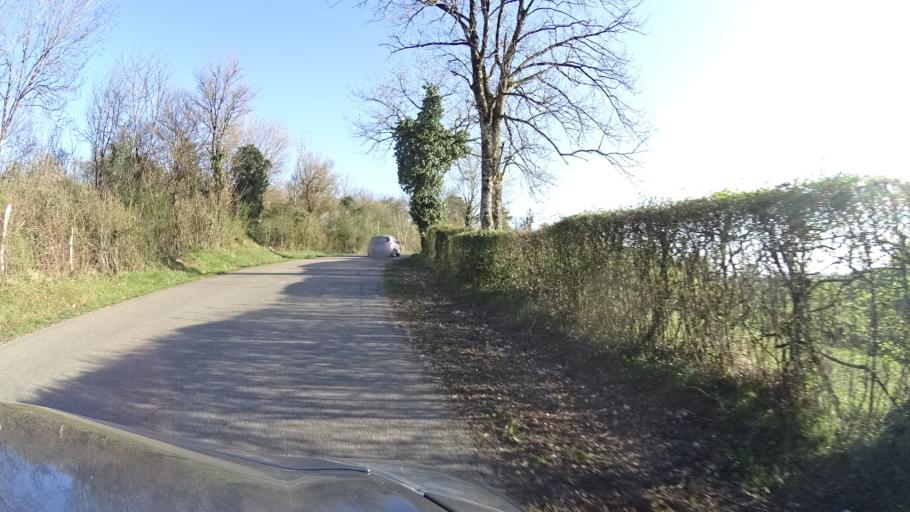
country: FR
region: Franche-Comte
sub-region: Departement du Doubs
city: Avanne-Aveney
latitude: 47.1925
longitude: 5.9853
